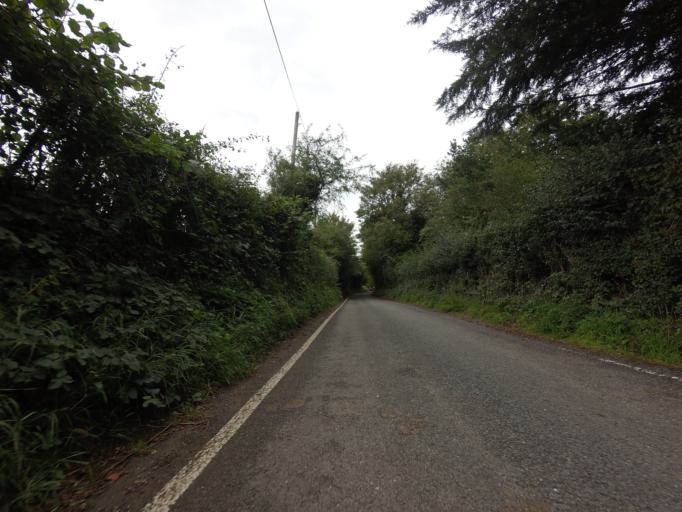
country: GB
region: England
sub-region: Hertfordshire
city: Reed
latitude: 51.9913
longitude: 0.0920
